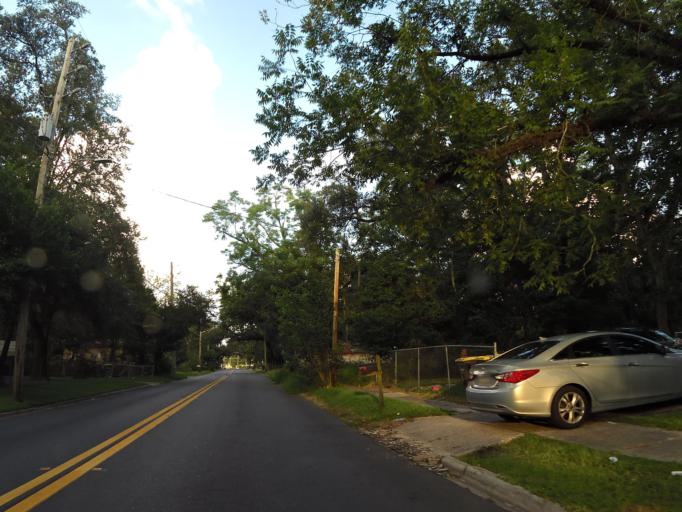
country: US
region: Florida
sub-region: Duval County
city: Jacksonville
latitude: 30.3365
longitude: -81.7020
